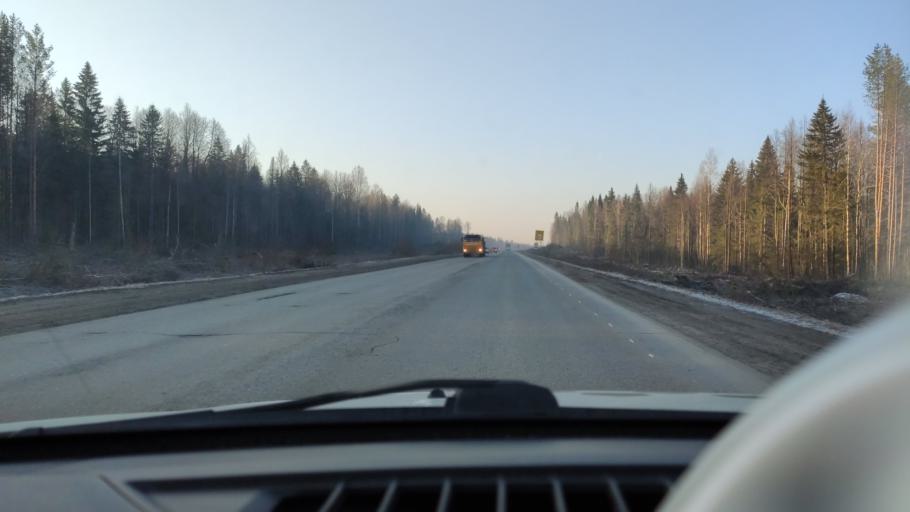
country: RU
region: Perm
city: Polazna
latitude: 58.1219
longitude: 56.4242
